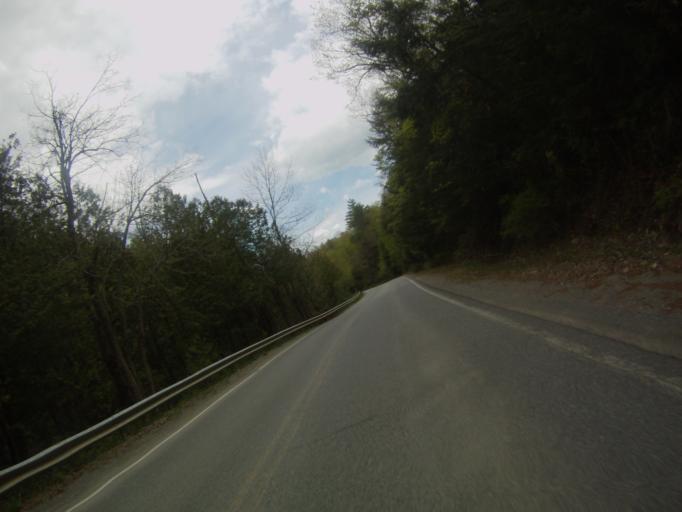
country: US
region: New York
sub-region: Essex County
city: Port Henry
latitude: 43.9465
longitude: -73.4965
